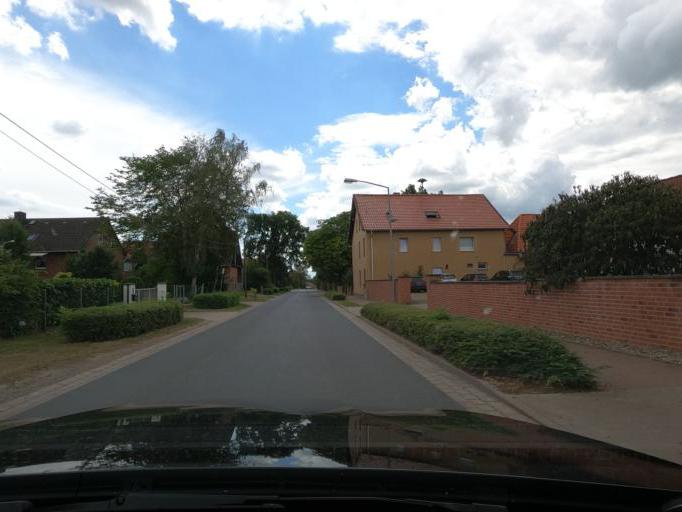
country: DE
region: Lower Saxony
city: Algermissen
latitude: 52.2842
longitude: 10.0143
